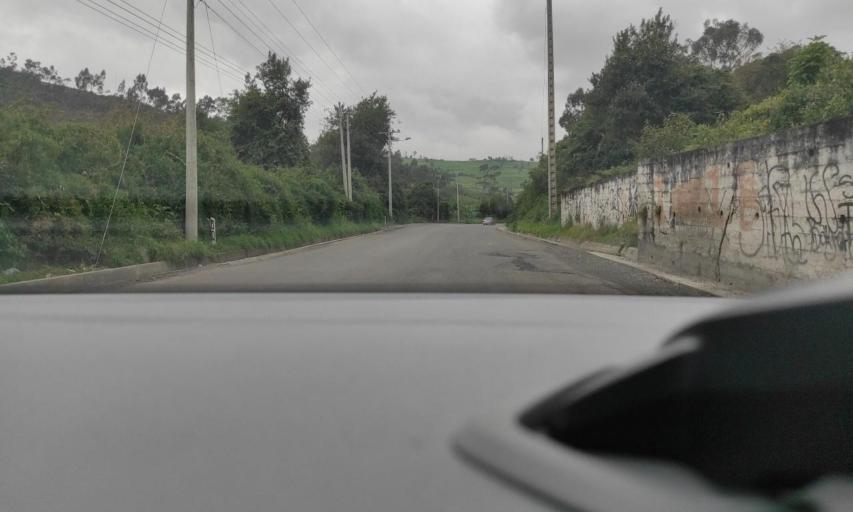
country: EC
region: Canar
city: Azogues
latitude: -2.6683
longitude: -78.8998
